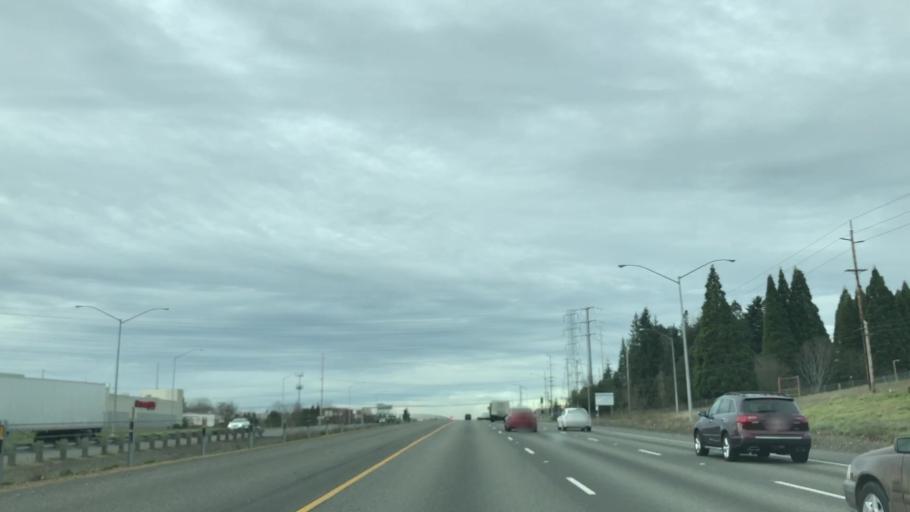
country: US
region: Oregon
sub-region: Washington County
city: Oak Hills
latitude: 45.5328
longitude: -122.8431
